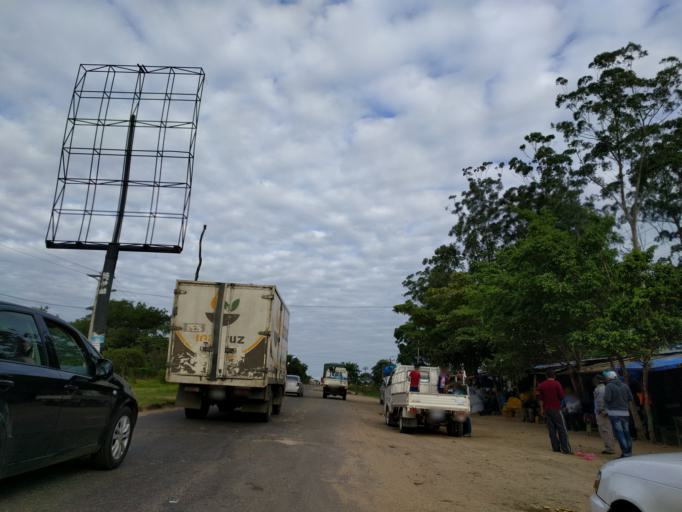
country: BO
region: Santa Cruz
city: Santa Rita
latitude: -17.8707
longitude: -63.2737
